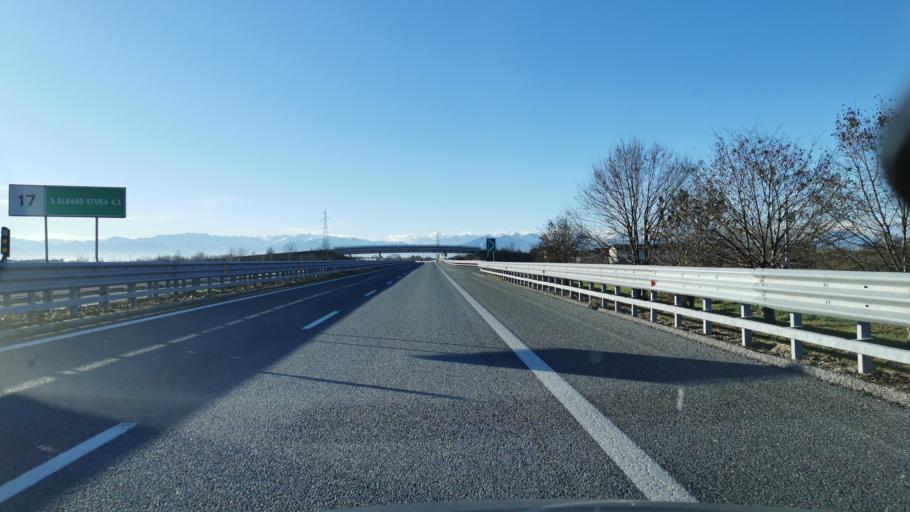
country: IT
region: Piedmont
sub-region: Provincia di Cuneo
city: Trinita
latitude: 44.4705
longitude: 7.7438
